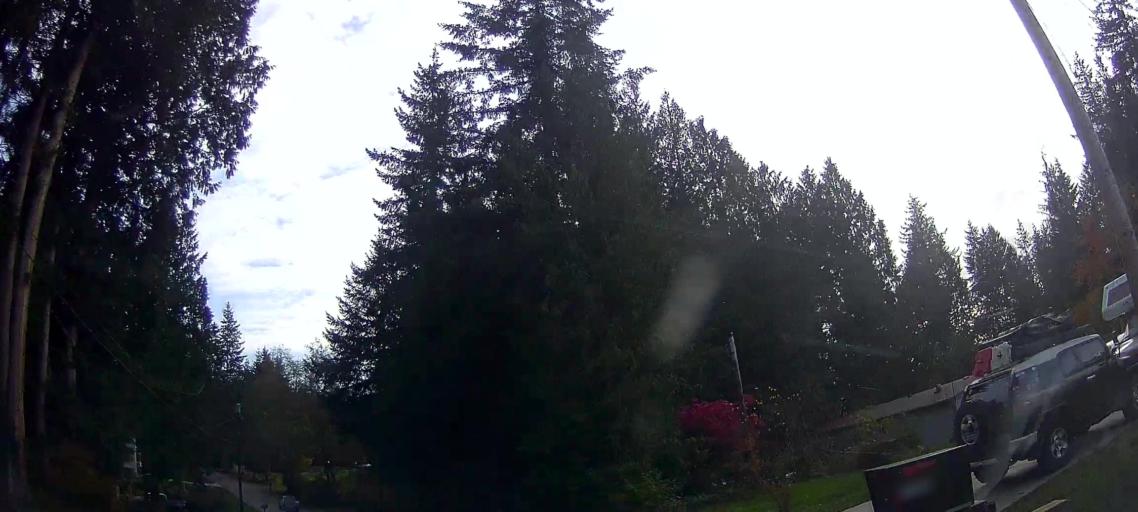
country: US
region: Washington
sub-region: Snohomish County
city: Stanwood
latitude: 48.2821
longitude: -122.3499
